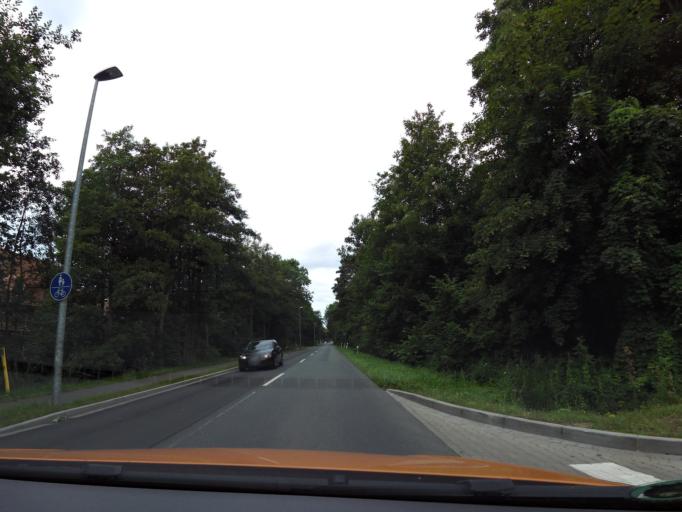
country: DE
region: Lower Saxony
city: Oldenburg
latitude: 53.1641
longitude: 8.1617
